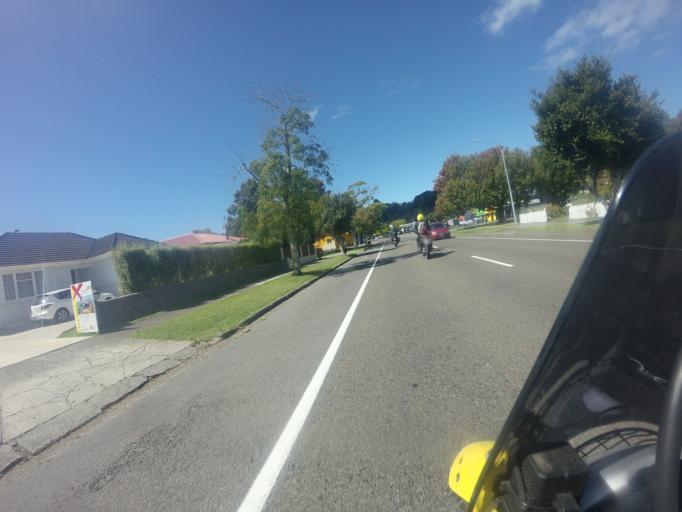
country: NZ
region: Bay of Plenty
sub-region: Whakatane District
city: Whakatane
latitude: -37.9536
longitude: 176.9888
